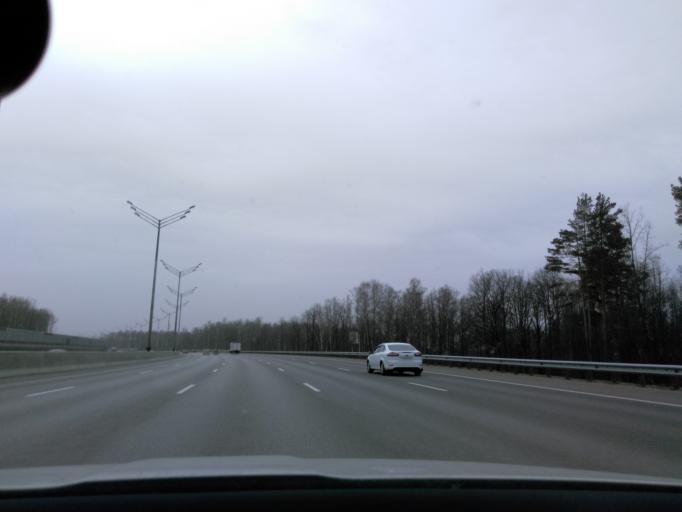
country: RU
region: Moscow
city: Khimki
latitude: 55.9207
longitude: 37.4559
